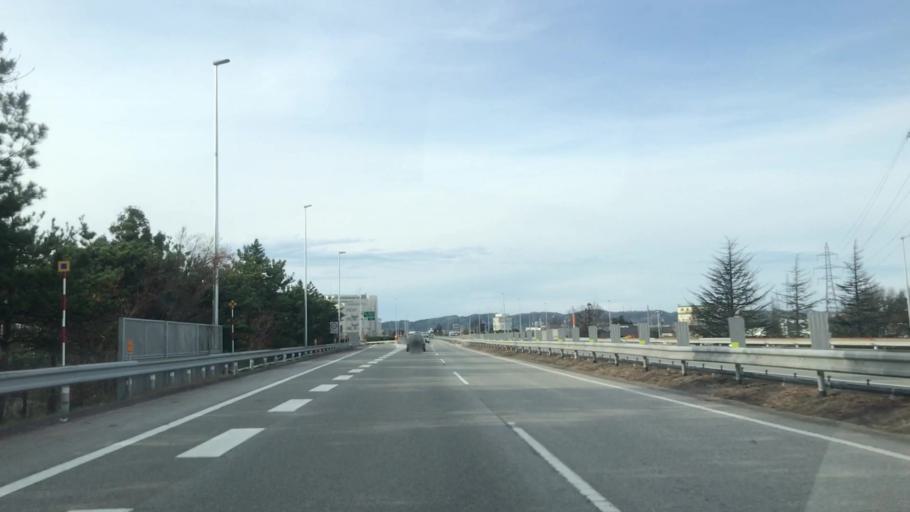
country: JP
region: Toyama
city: Toyama-shi
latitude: 36.6542
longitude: 137.2071
